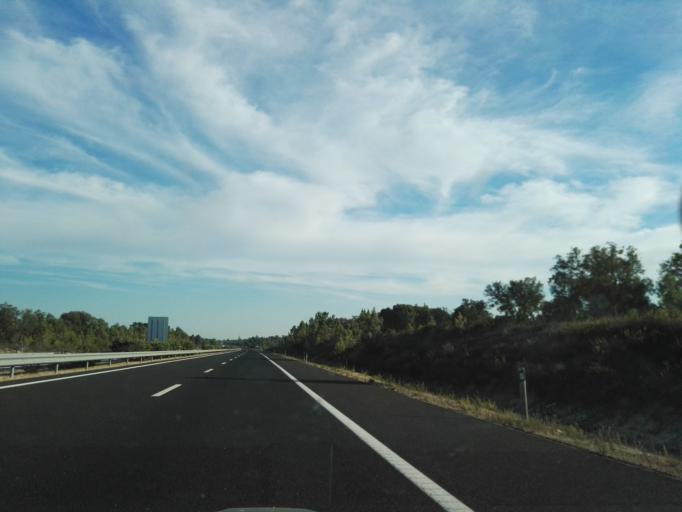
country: PT
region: Santarem
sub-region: Benavente
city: Poceirao
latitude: 38.8265
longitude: -8.7169
